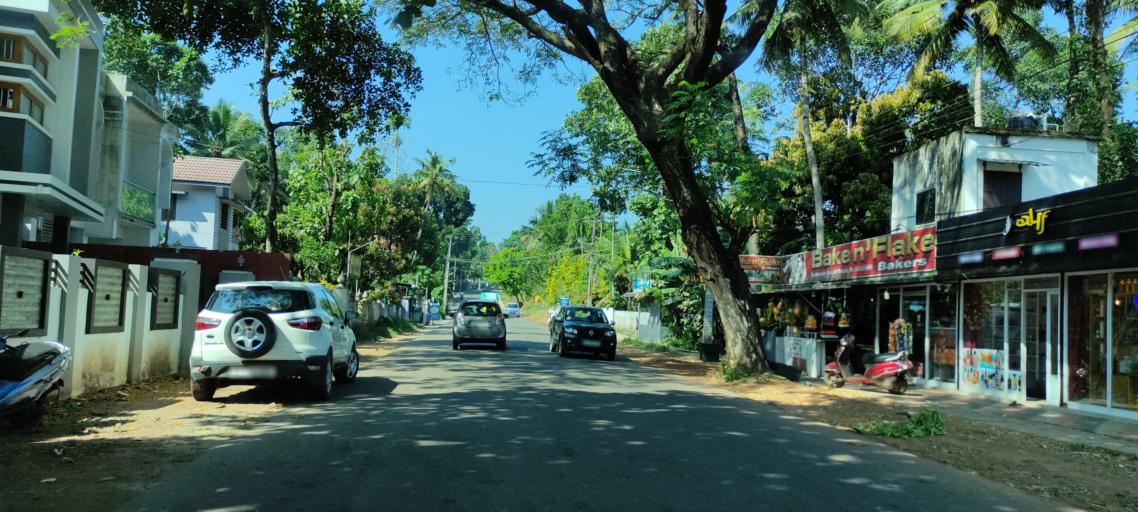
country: IN
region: Kerala
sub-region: Kollam
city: Panmana
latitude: 9.0422
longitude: 76.6128
